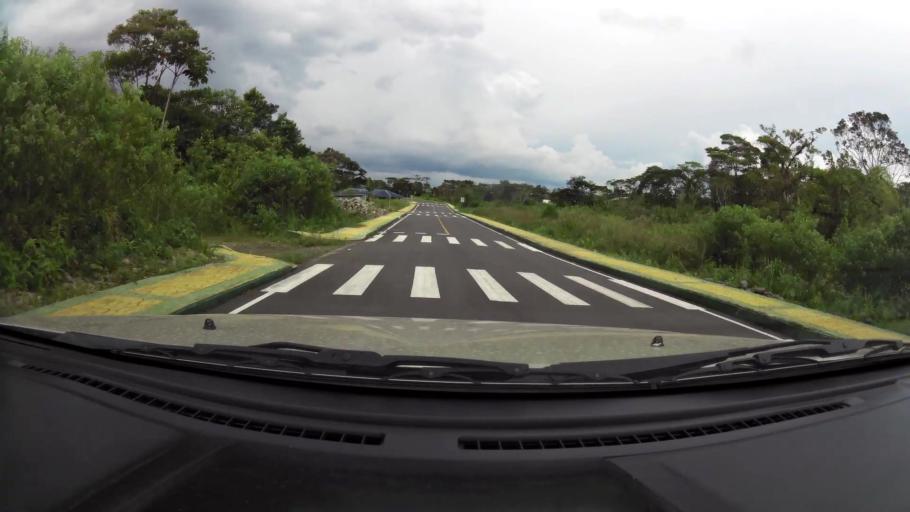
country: EC
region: Pastaza
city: Puyo
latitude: -1.5028
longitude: -78.0190
